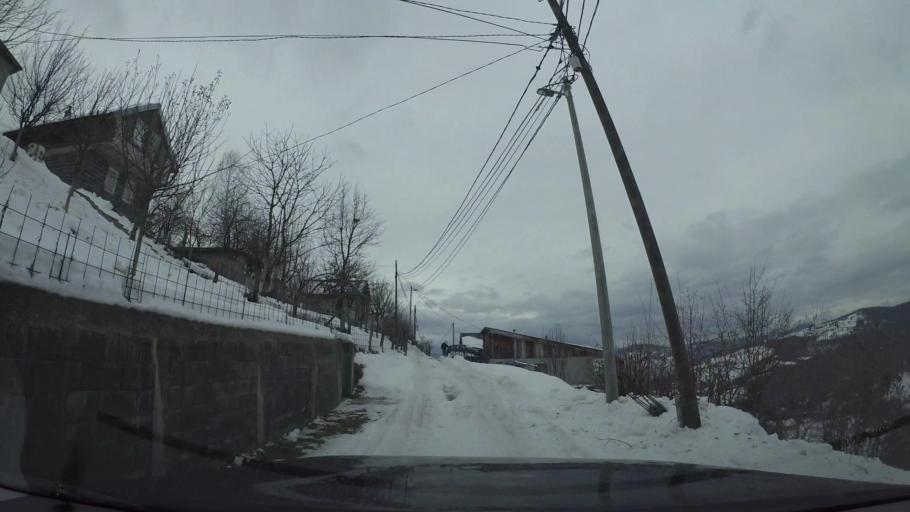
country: BA
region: Federation of Bosnia and Herzegovina
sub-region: Kanton Sarajevo
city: Sarajevo
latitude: 43.8643
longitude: 18.3532
